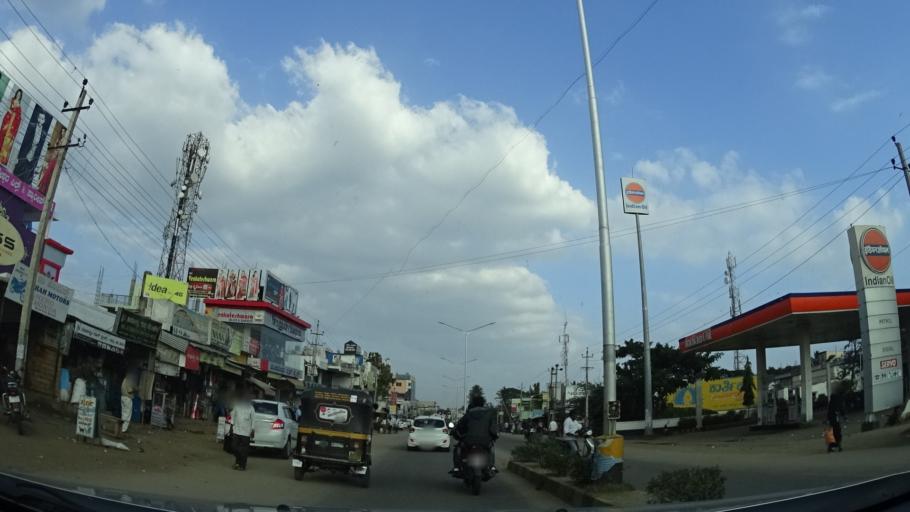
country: IN
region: Karnataka
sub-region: Mandya
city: Malavalli
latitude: 12.3857
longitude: 77.0577
